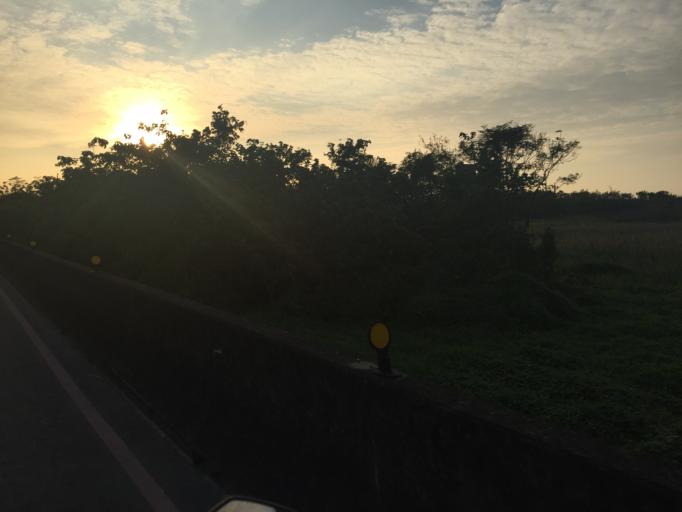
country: TW
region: Taiwan
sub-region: Hsinchu
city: Hsinchu
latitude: 24.7428
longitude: 120.8960
